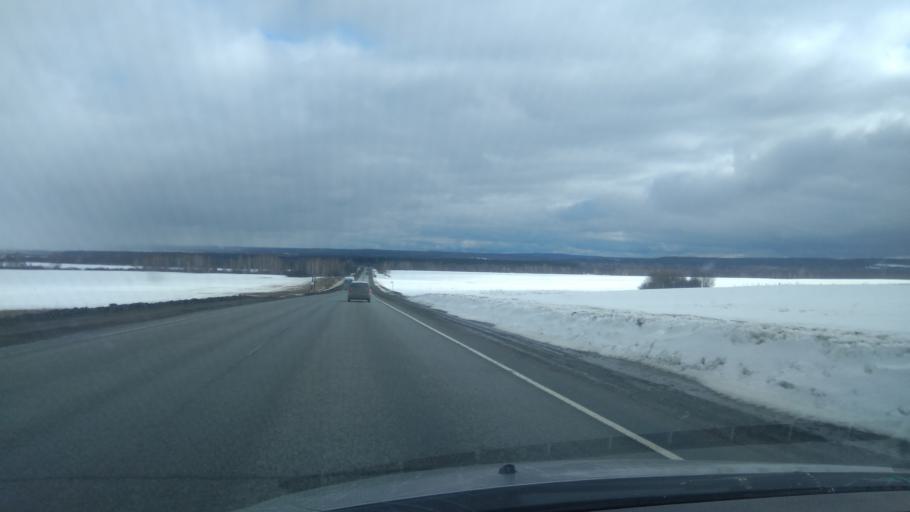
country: RU
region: Sverdlovsk
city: Ufimskiy
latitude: 56.7733
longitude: 58.0636
